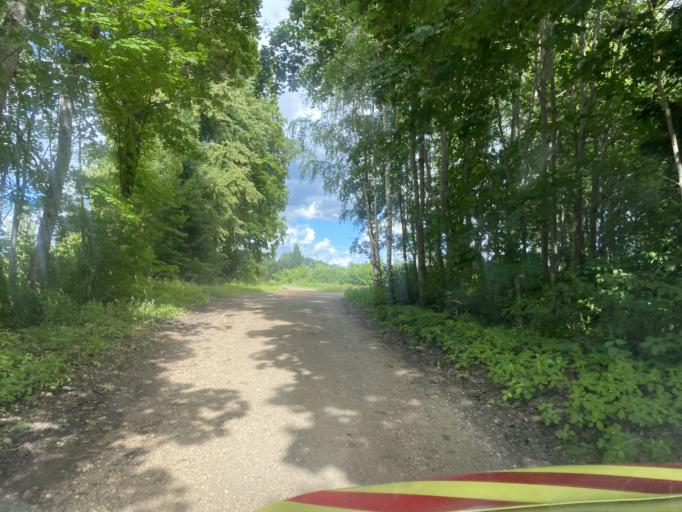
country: EE
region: Viljandimaa
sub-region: Viiratsi vald
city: Viiratsi
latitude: 58.4016
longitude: 25.8031
